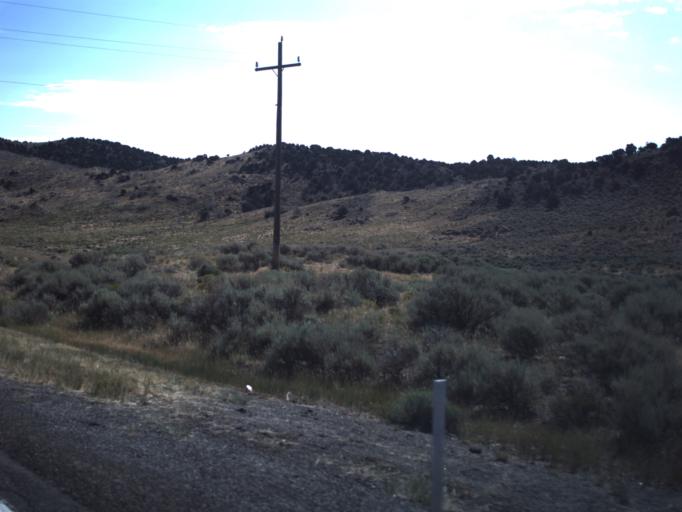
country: US
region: Utah
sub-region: Utah County
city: Genola
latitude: 39.9642
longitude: -112.0957
